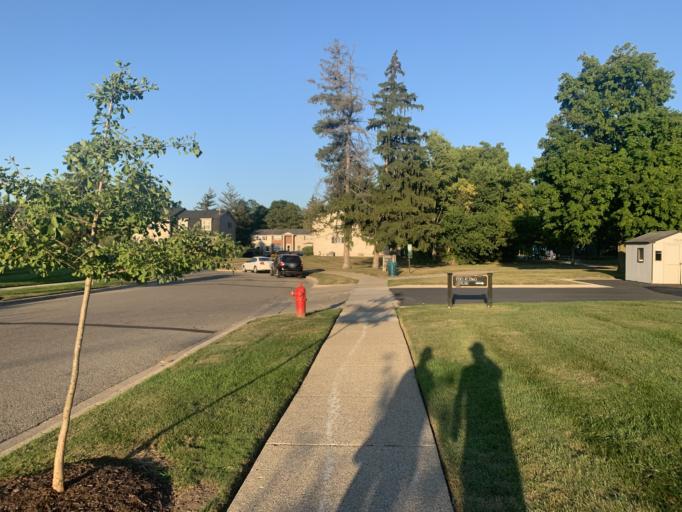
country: US
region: Michigan
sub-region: Washtenaw County
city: Ann Arbor
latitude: 42.2571
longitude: -83.7325
